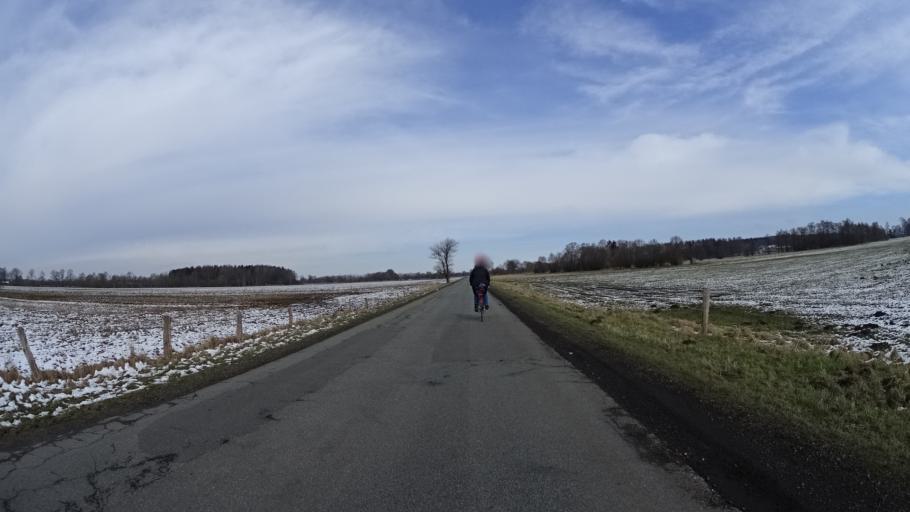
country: DE
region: Schleswig-Holstein
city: Gonnebek
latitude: 54.0439
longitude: 10.1290
